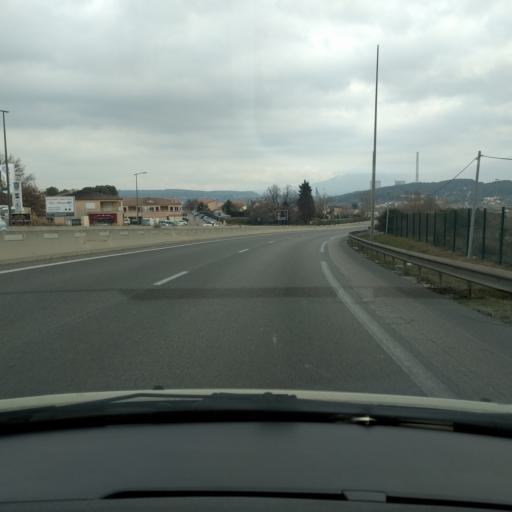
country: FR
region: Provence-Alpes-Cote d'Azur
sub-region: Departement des Bouches-du-Rhone
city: Gardanne
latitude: 43.4532
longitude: 5.4537
